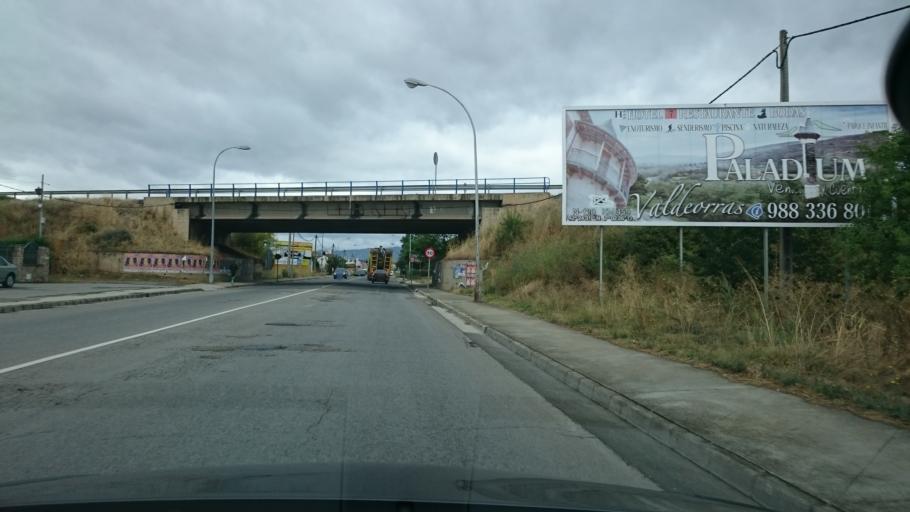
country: ES
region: Castille and Leon
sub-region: Provincia de Leon
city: Camponaraya
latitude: 42.5649
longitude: -6.6354
